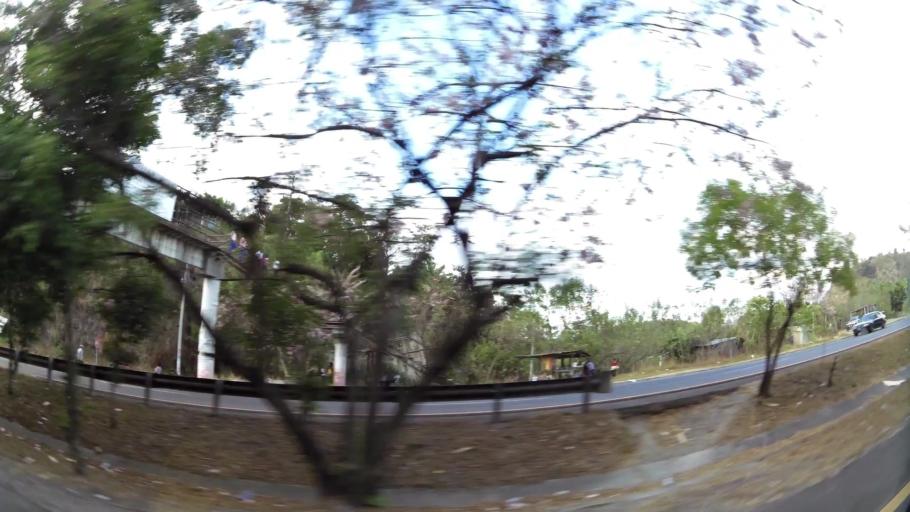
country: SV
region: Cuscatlan
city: Cojutepeque
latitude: 13.7238
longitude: -88.9044
